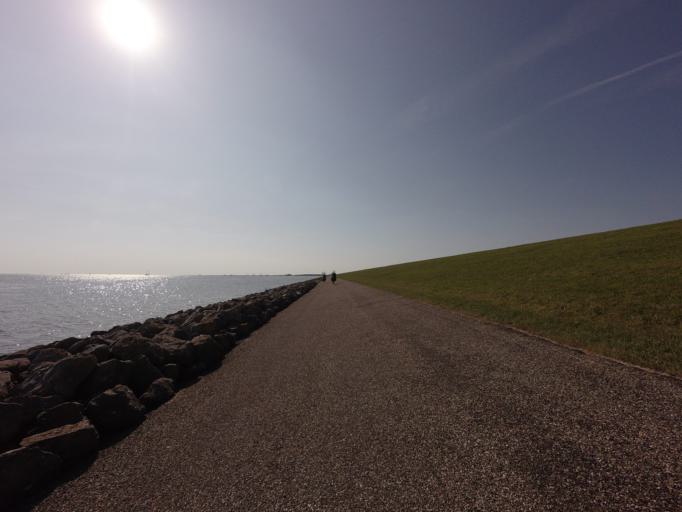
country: NL
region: Friesland
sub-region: Gemeente Schiermonnikoog
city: Schiermonnikoog
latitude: 53.4724
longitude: 6.1888
